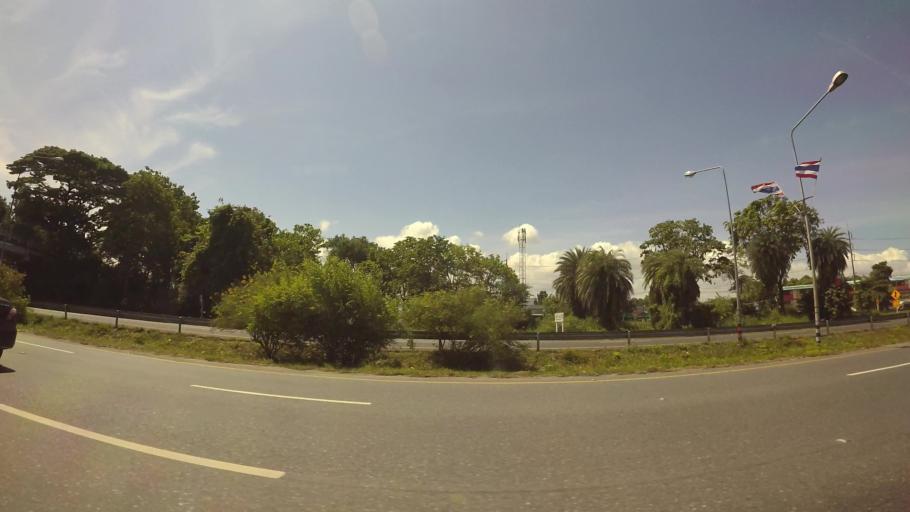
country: TH
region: Chon Buri
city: Chon Buri
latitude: 13.3334
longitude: 100.9694
